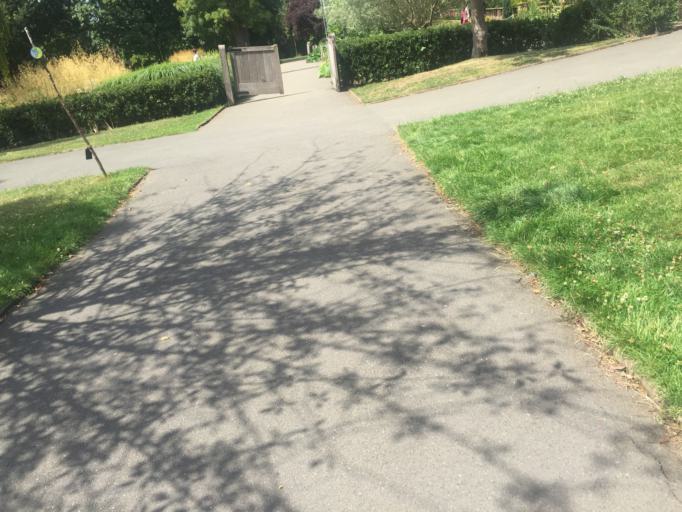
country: GB
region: England
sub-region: Greater London
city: Catford
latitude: 51.4413
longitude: -0.0621
